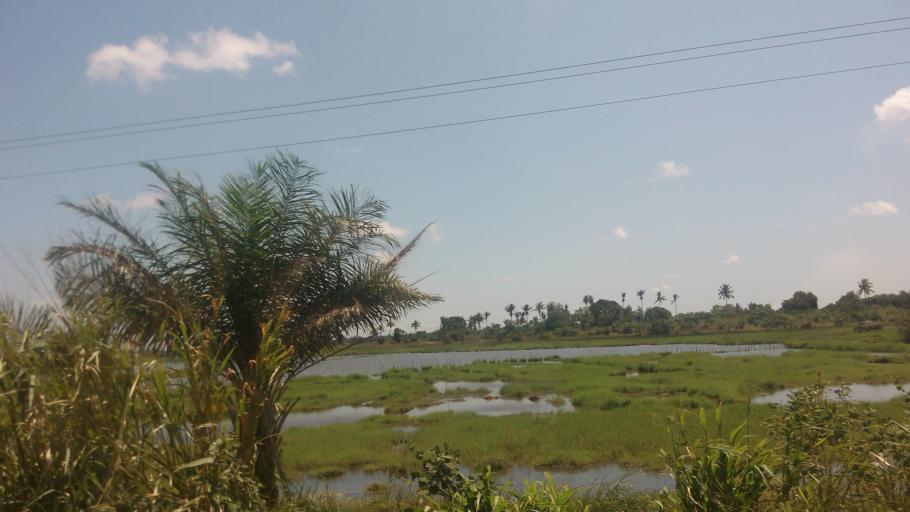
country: BJ
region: Mono
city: Come
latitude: 6.3976
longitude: 1.9257
